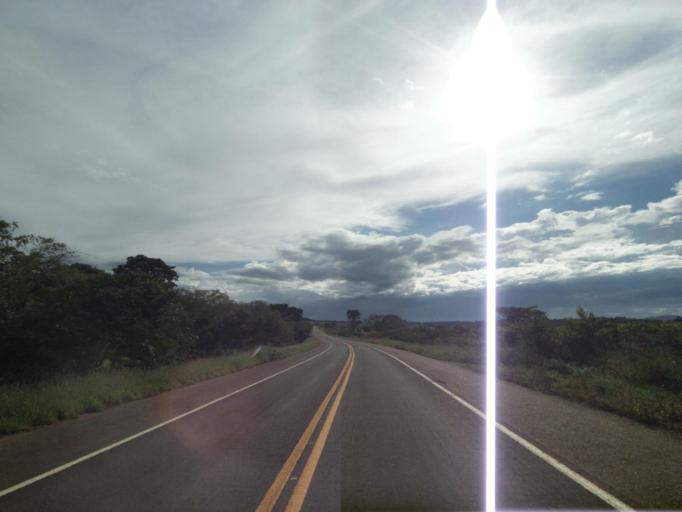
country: BR
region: Goias
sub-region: Jaragua
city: Jaragua
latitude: -15.8927
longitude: -49.5167
